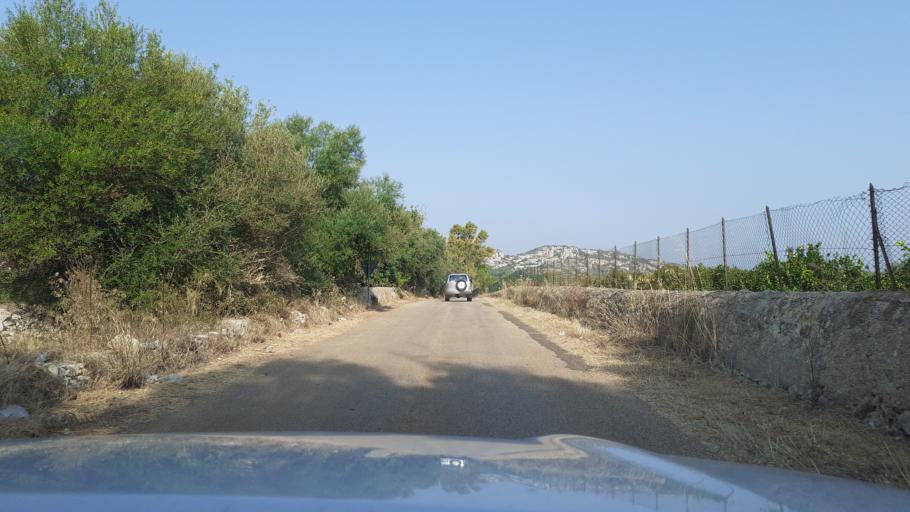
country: IT
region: Sicily
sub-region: Provincia di Siracusa
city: Cassibile
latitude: 36.9746
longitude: 15.1877
